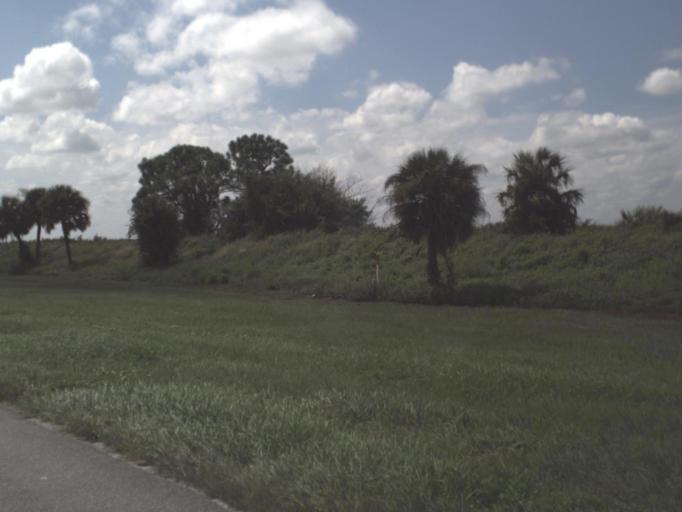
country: US
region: Florida
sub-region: Hendry County
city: Port LaBelle
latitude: 26.6115
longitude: -81.4366
